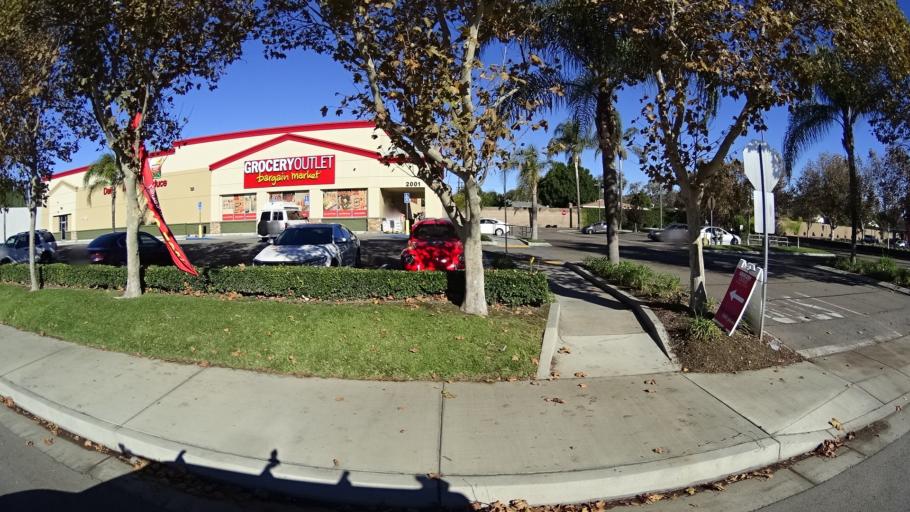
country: US
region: California
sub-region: Orange County
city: La Habra
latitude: 33.9400
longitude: -117.9684
